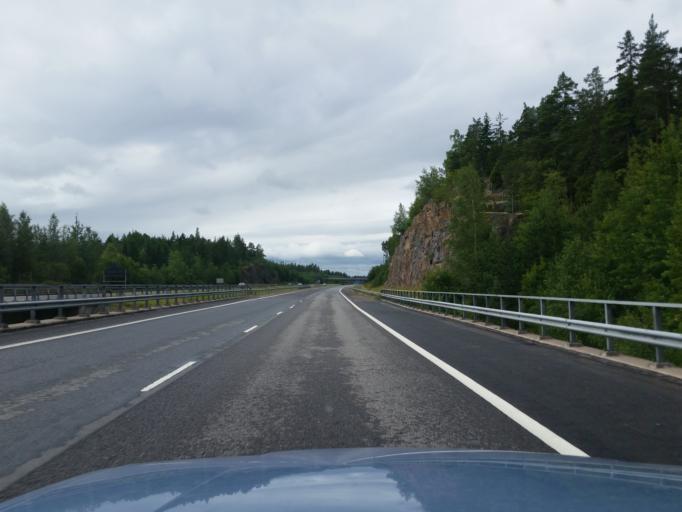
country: FI
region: Varsinais-Suomi
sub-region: Turku
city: Piikkioe
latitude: 60.4350
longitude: 22.4577
